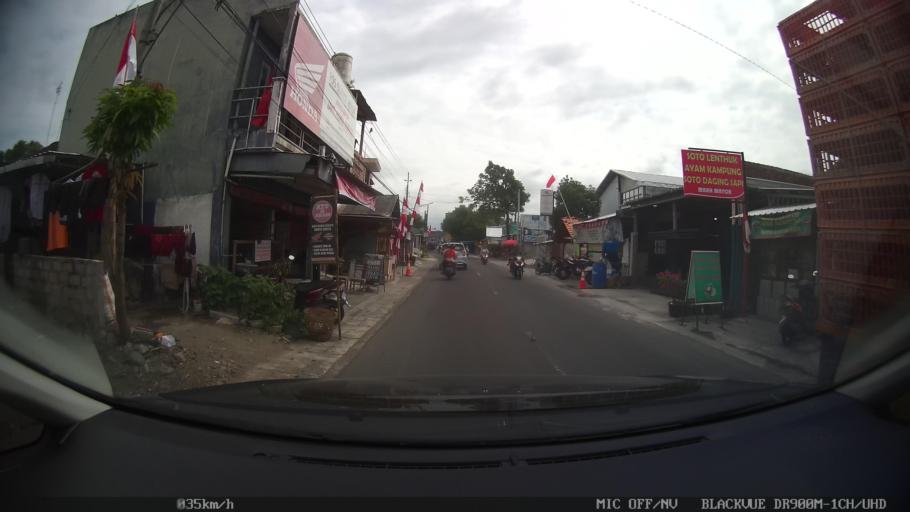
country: ID
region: Daerah Istimewa Yogyakarta
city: Depok
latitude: -7.8065
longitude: 110.4435
